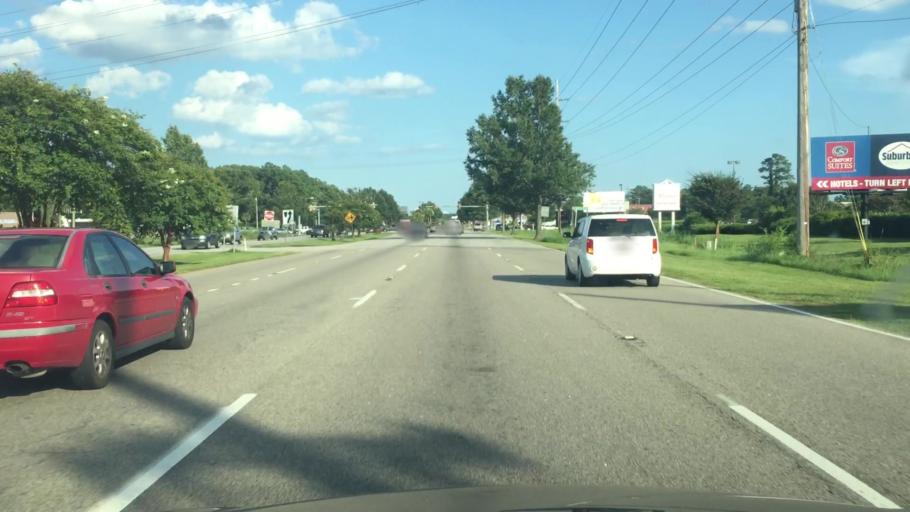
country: US
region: South Carolina
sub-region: Horry County
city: Myrtle Beach
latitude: 33.7077
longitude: -78.9125
